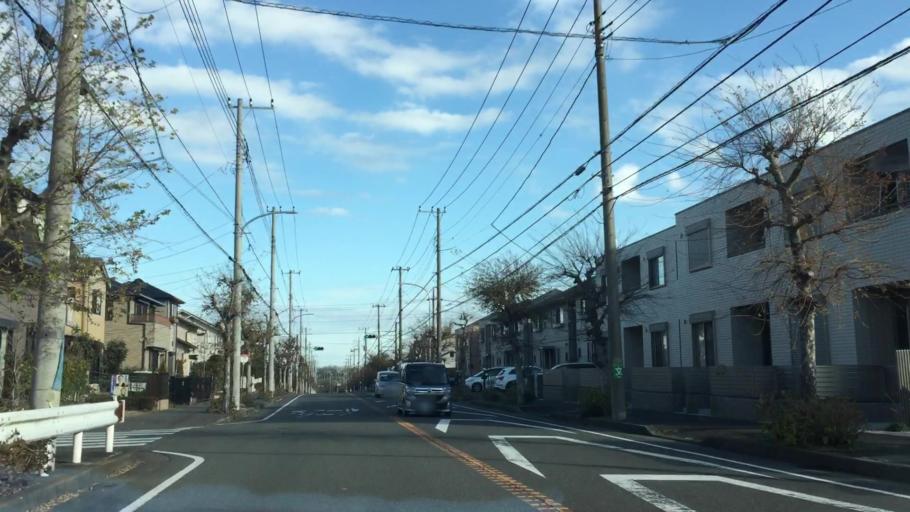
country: JP
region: Kanagawa
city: Zushi
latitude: 35.3378
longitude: 139.5995
